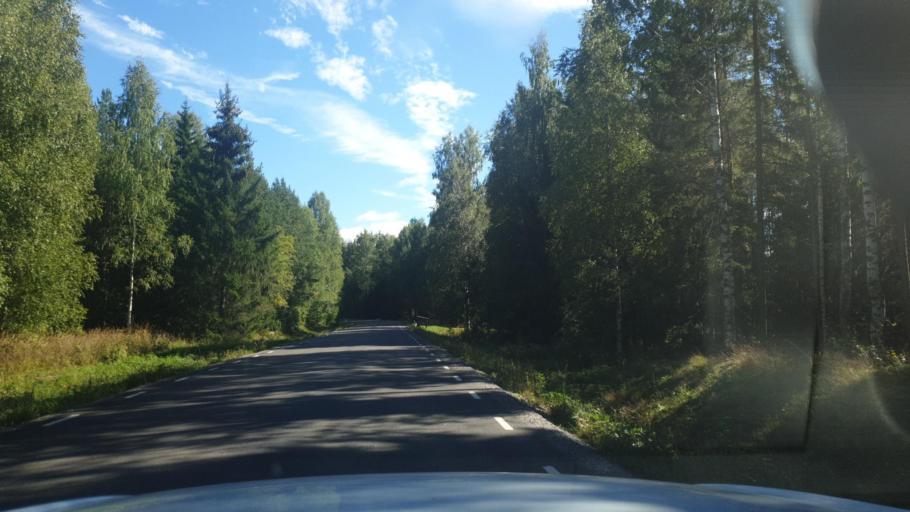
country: SE
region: Vaermland
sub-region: Torsby Kommun
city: Torsby
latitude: 60.0025
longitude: 12.7238
